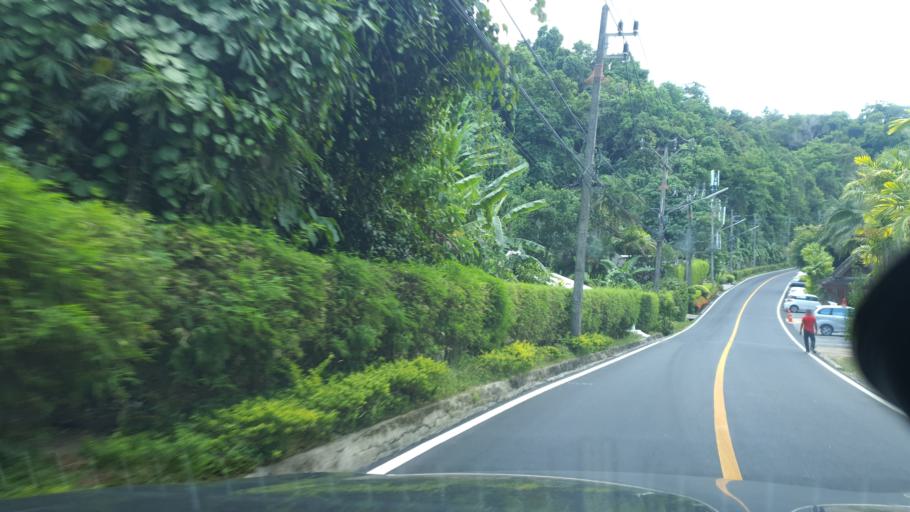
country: TH
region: Phuket
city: Thalang
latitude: 8.0475
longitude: 98.2785
